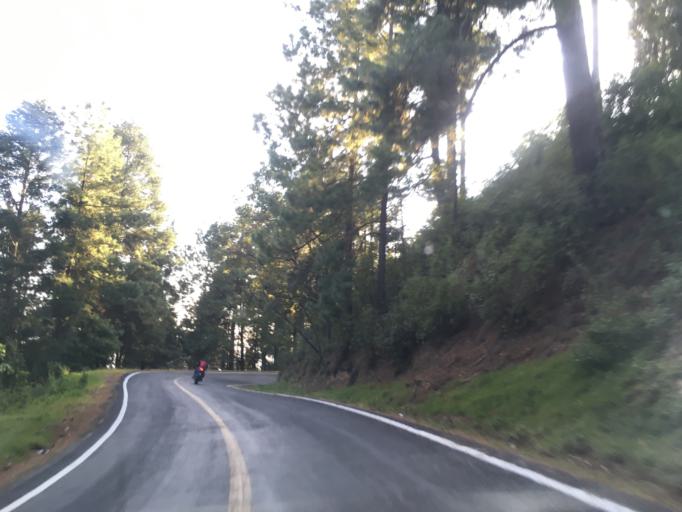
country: MX
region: Michoacan
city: Tzitzio
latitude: 19.6823
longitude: -100.8838
